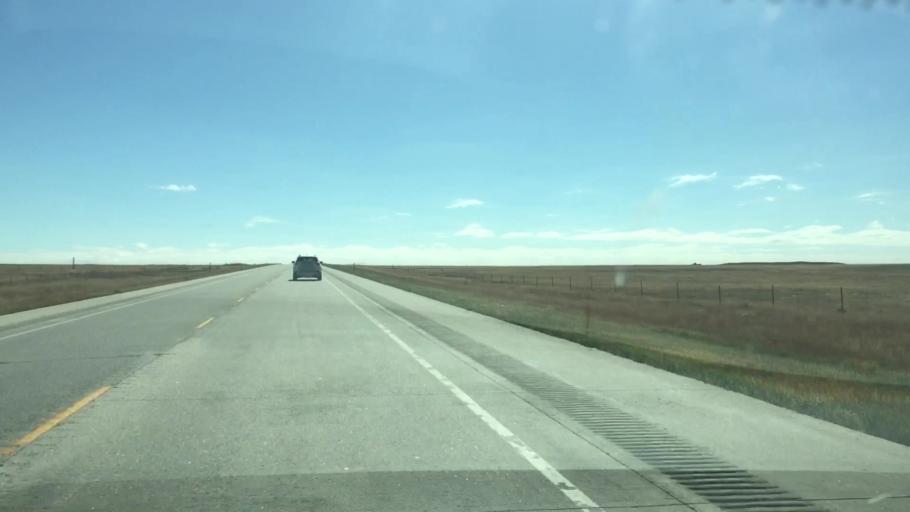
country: US
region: Colorado
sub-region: Lincoln County
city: Hugo
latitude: 39.1824
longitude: -103.5491
